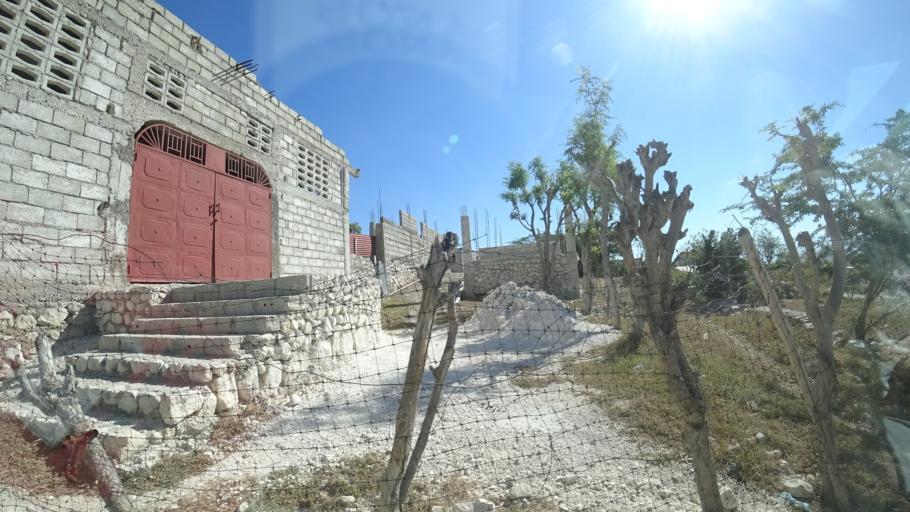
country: HT
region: Ouest
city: Croix des Bouquets
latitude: 18.6762
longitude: -72.2395
